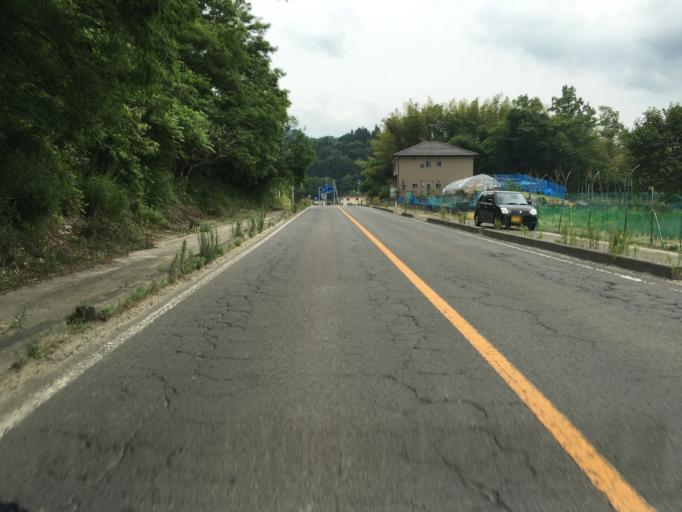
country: JP
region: Fukushima
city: Hobaramachi
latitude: 37.6686
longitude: 140.6131
